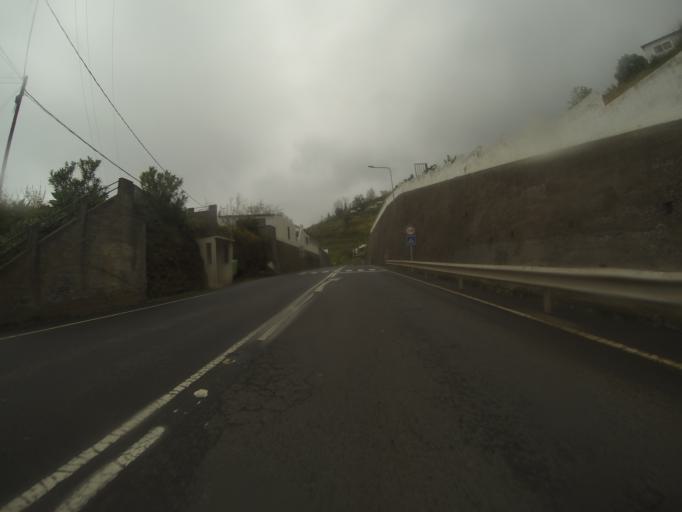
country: PT
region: Madeira
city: Canico
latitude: 32.6476
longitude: -16.8658
